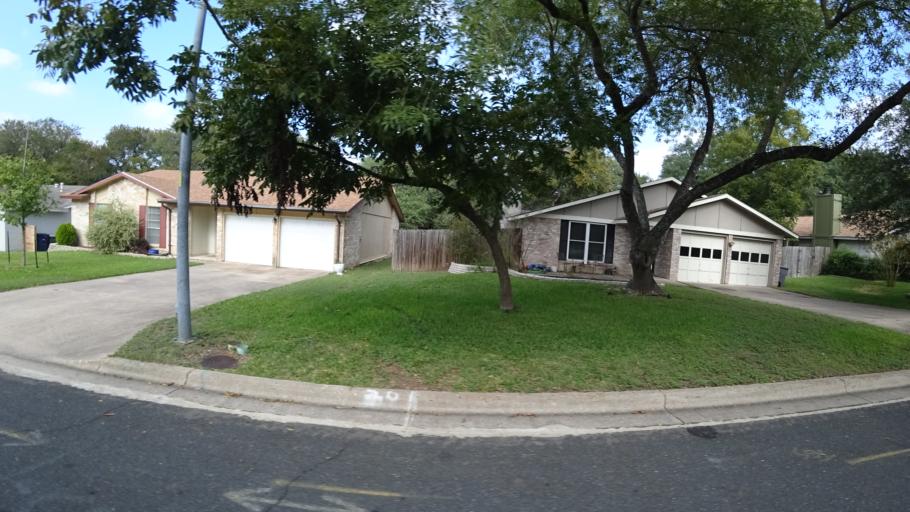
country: US
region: Texas
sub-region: Travis County
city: Shady Hollow
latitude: 30.2000
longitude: -97.8175
